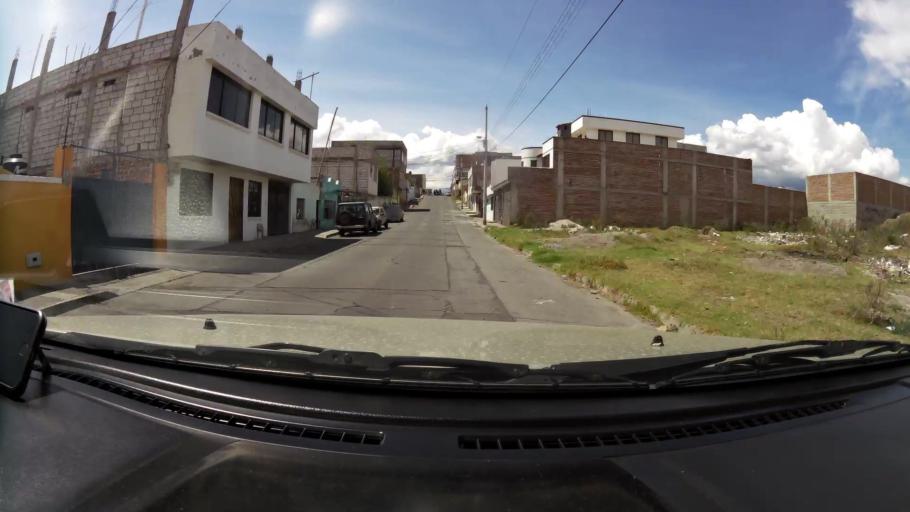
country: EC
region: Chimborazo
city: Riobamba
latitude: -1.6595
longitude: -78.6435
